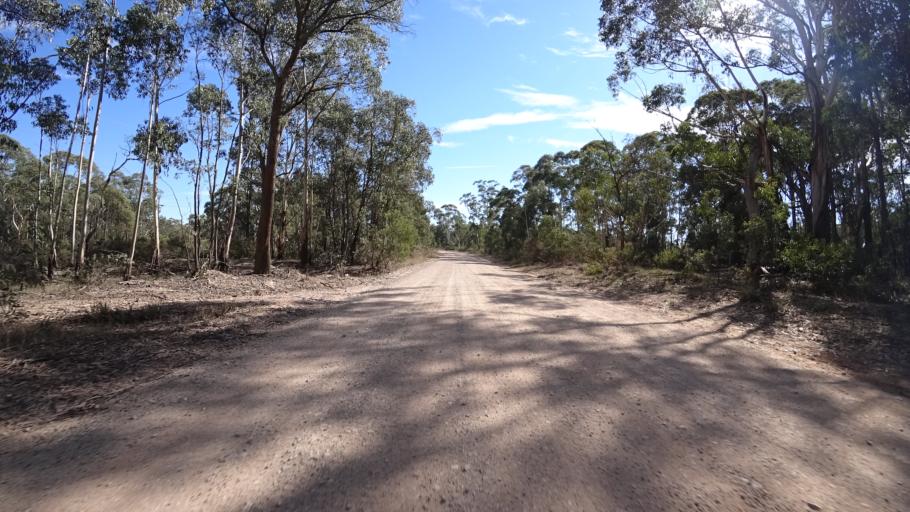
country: AU
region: New South Wales
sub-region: Lithgow
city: Lithgow
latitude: -33.4185
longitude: 150.2042
